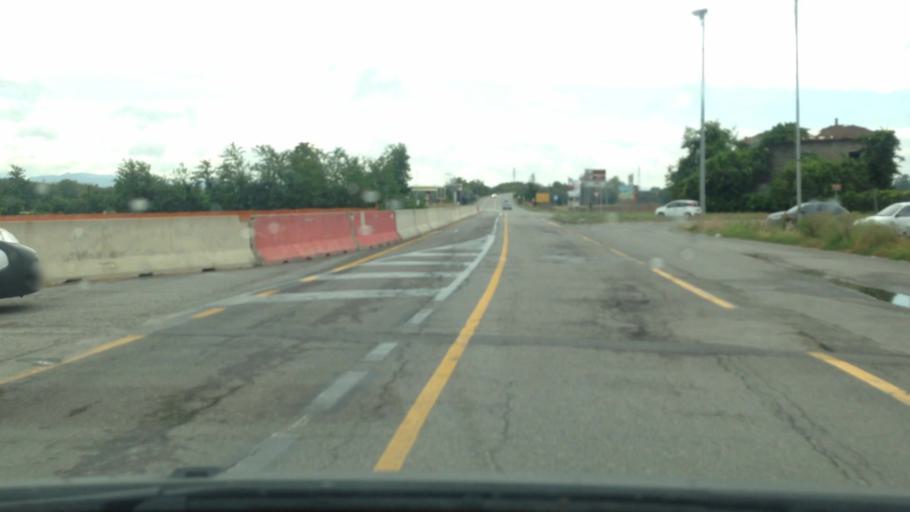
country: IT
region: Piedmont
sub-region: Provincia di Alessandria
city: Tortona
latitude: 44.9028
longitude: 8.8382
